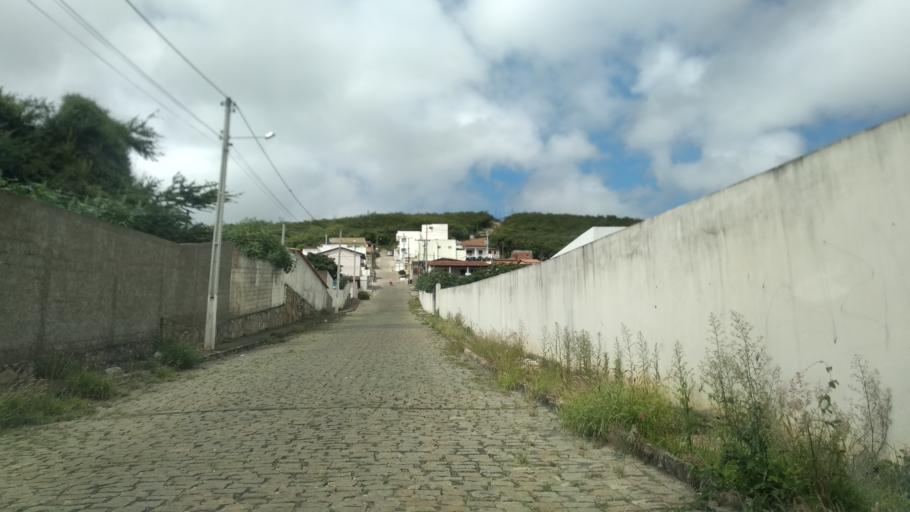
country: BR
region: Bahia
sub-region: Caetite
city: Caetite
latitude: -14.0680
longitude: -42.4943
